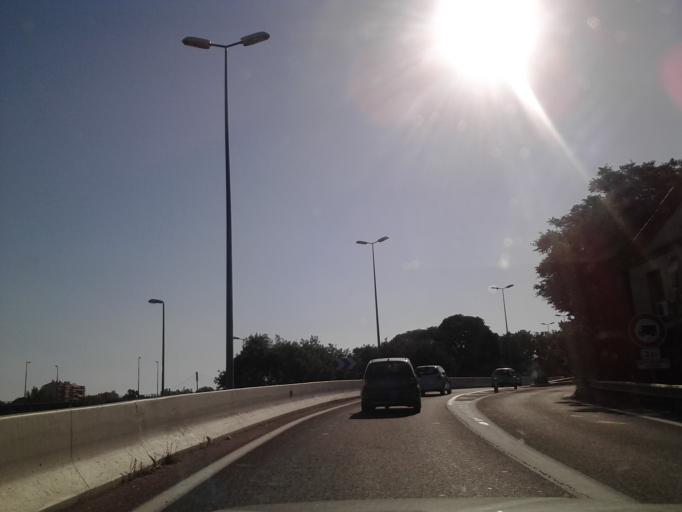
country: FR
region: Languedoc-Roussillon
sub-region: Departement des Pyrenees-Orientales
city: Perpignan
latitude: 42.7011
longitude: 2.8836
